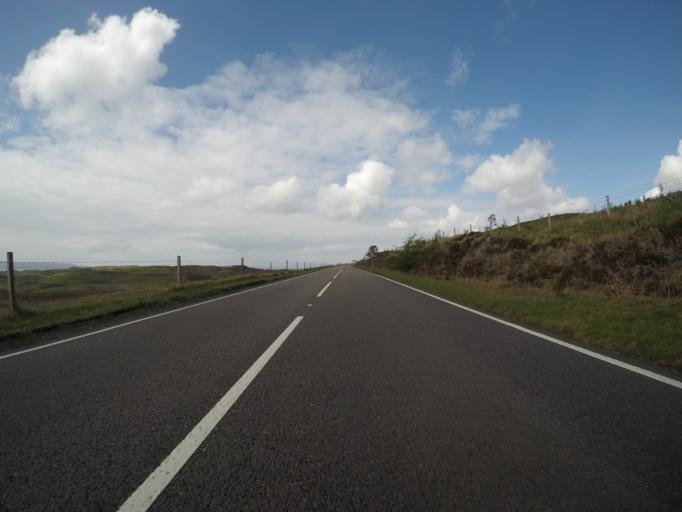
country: GB
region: Scotland
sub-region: Highland
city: Portree
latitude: 57.5501
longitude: -6.3641
